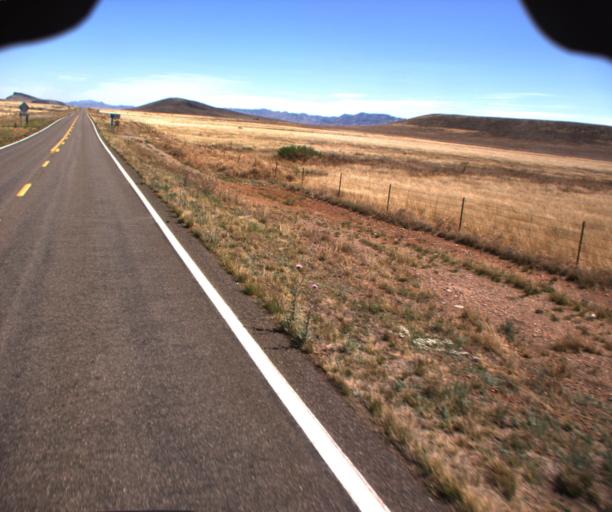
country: US
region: Arizona
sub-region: Cochise County
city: Douglas
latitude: 31.5999
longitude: -109.2328
